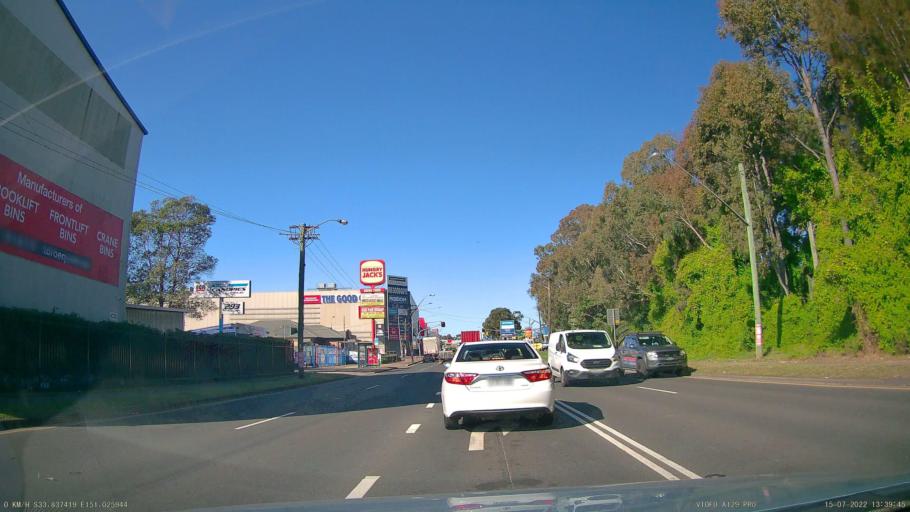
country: AU
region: New South Wales
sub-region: Parramatta
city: Granville
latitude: -33.8372
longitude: 151.0264
